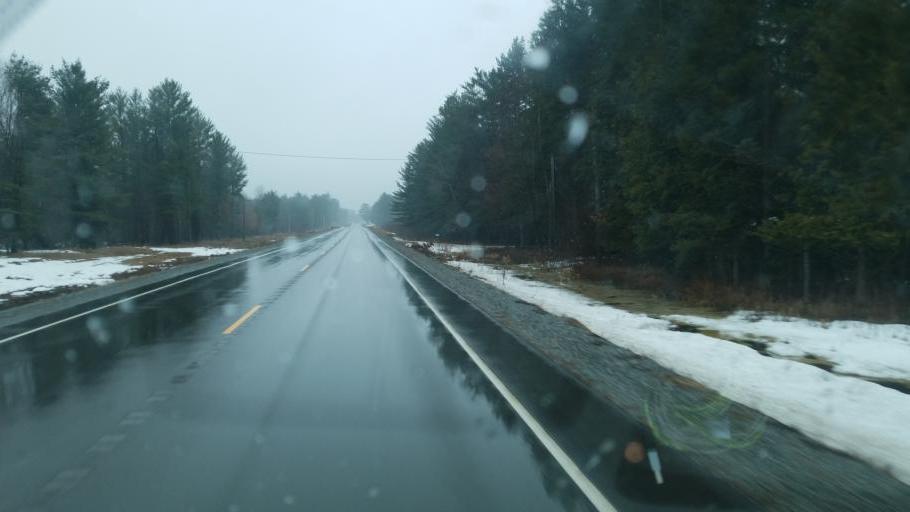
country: US
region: Wisconsin
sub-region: Clark County
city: Neillsville
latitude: 44.4842
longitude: -90.3558
